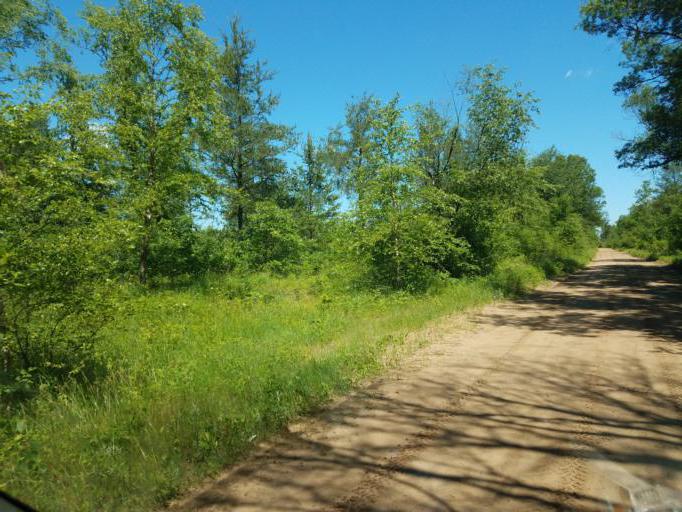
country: US
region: Wisconsin
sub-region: Adams County
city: Friendship
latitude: 44.0331
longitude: -89.9957
